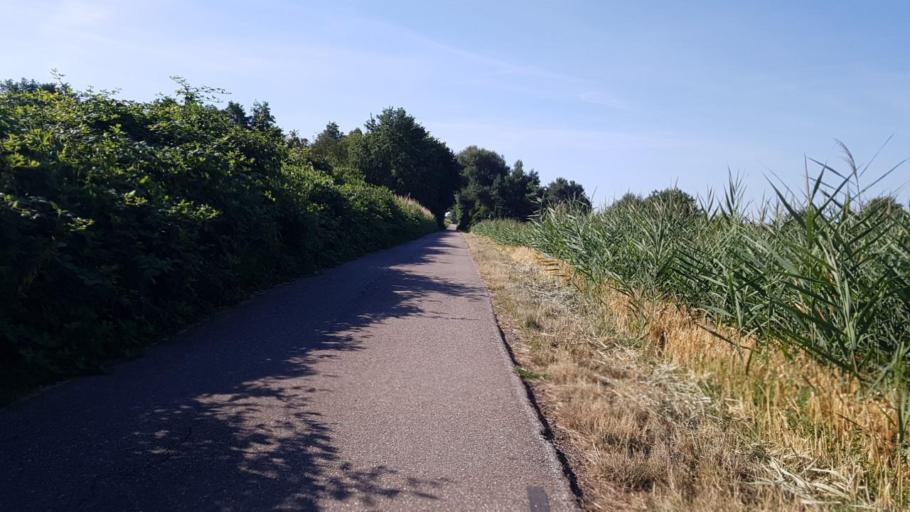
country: DE
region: Baden-Wuerttemberg
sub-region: Karlsruhe Region
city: Sankt Leon-Rot
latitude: 49.2818
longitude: 8.6132
